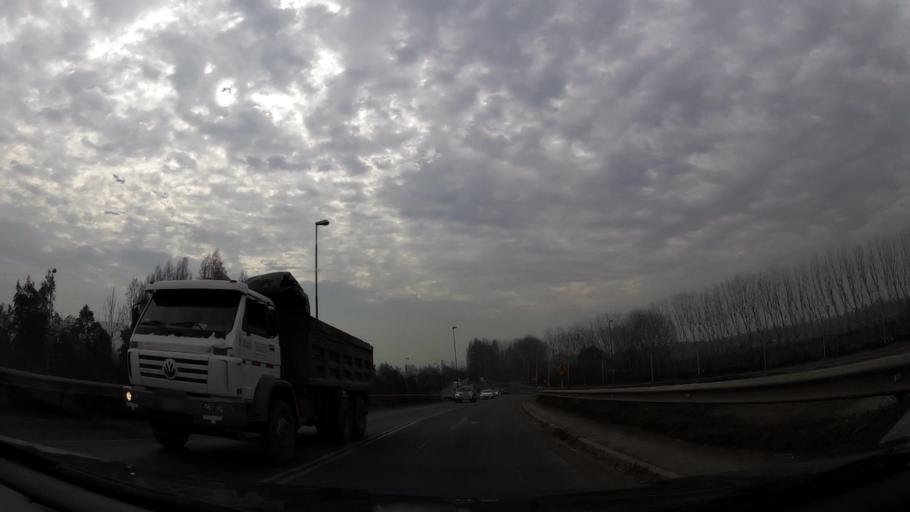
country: CL
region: Santiago Metropolitan
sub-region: Provincia de Chacabuco
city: Chicureo Abajo
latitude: -33.2403
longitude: -70.7561
